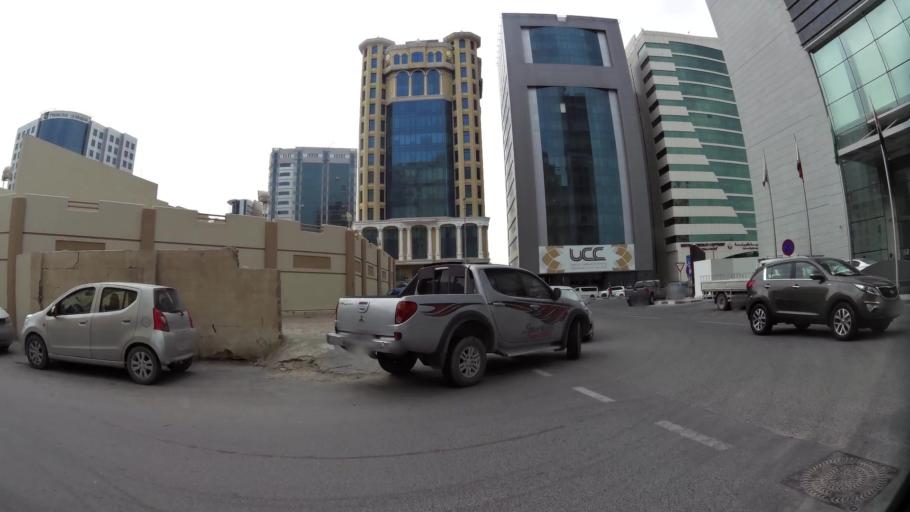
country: QA
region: Baladiyat ad Dawhah
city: Doha
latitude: 25.2881
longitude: 51.5451
